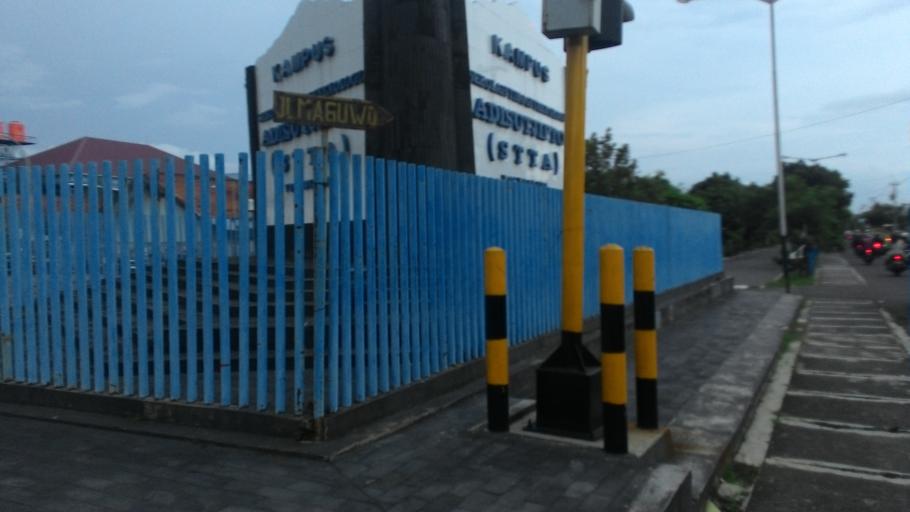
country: ID
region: Daerah Istimewa Yogyakarta
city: Depok
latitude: -7.7985
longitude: 110.4101
